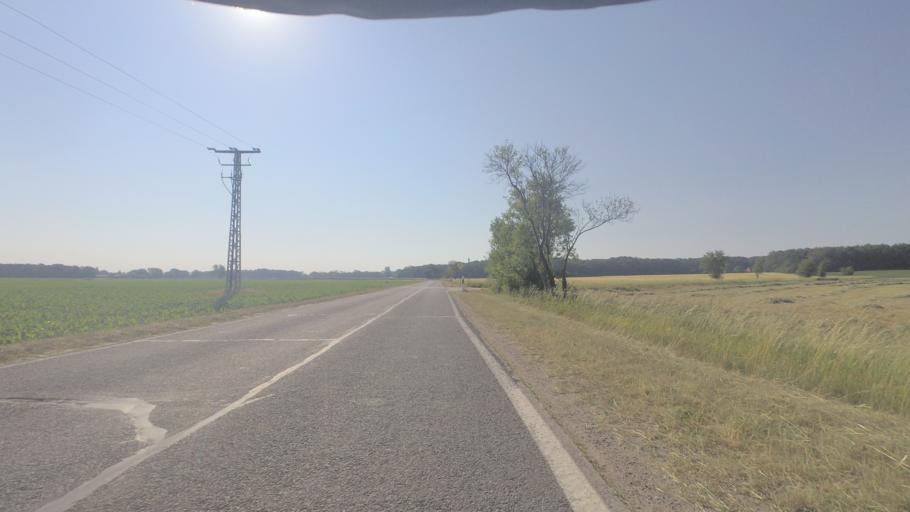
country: DE
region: Saxony-Anhalt
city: Quellendorf
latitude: 51.8153
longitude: 12.1288
